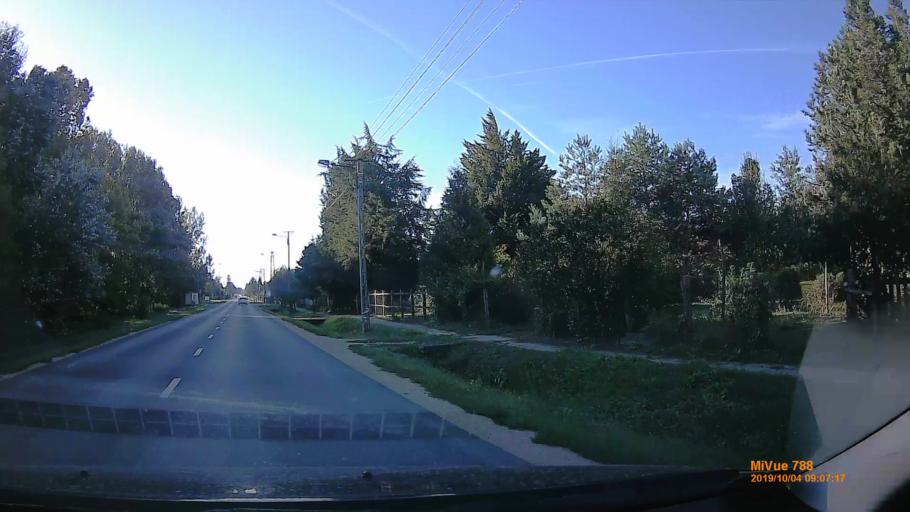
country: HU
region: Somogy
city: Karad
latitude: 46.6798
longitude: 17.7735
